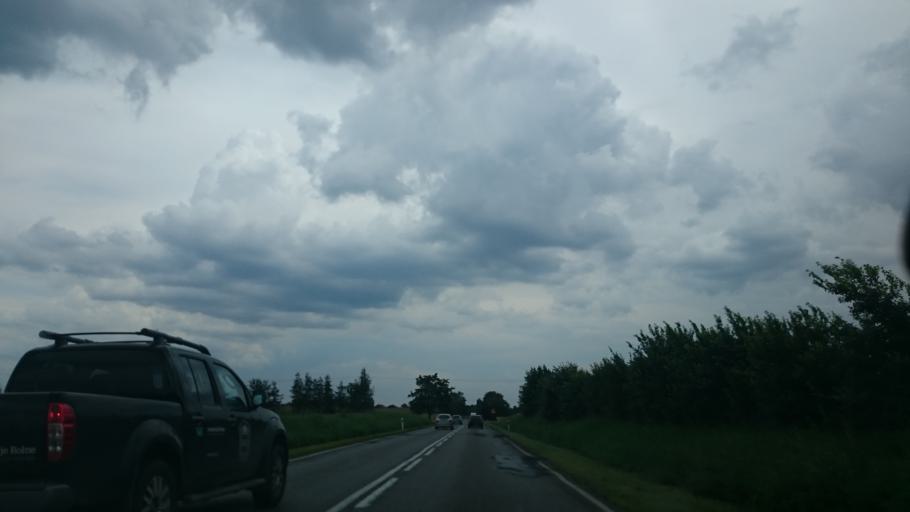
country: PL
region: Kujawsko-Pomorskie
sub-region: Powiat tucholski
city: Cekcyn
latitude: 53.5137
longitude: 17.9689
